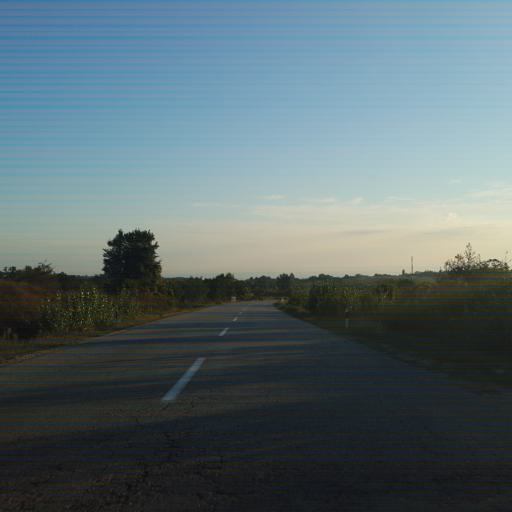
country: RS
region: Central Serbia
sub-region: Borski Okrug
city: Negotin
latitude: 44.2127
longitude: 22.4652
